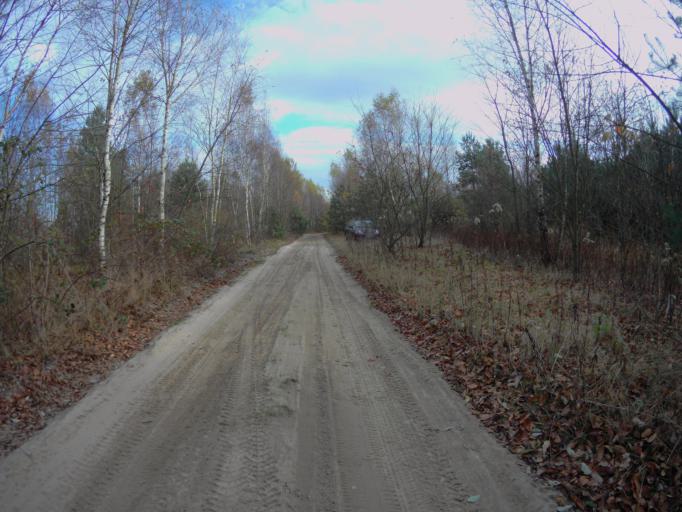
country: PL
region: Subcarpathian Voivodeship
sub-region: Powiat kolbuszowski
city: Lipnica
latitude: 50.3254
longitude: 21.9379
